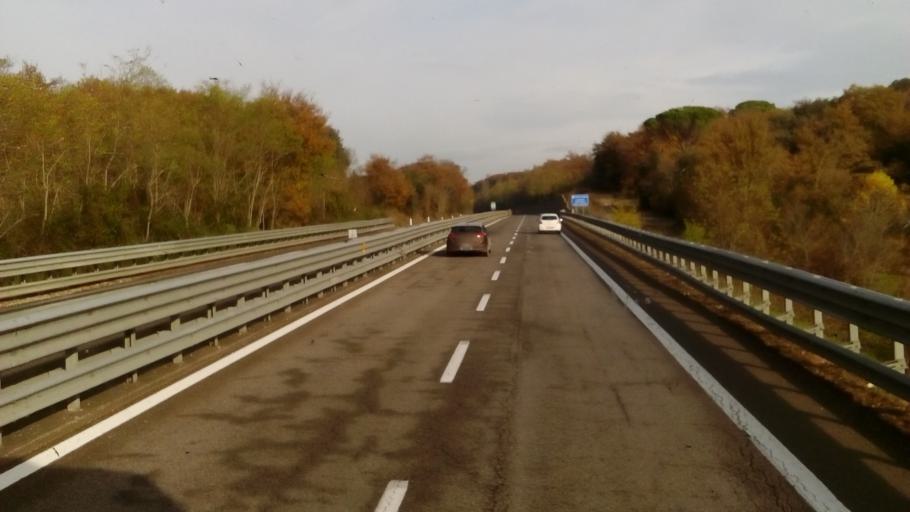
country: IT
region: Tuscany
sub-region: Provincia di Siena
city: Serre di Rapolano
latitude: 43.2743
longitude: 11.6294
